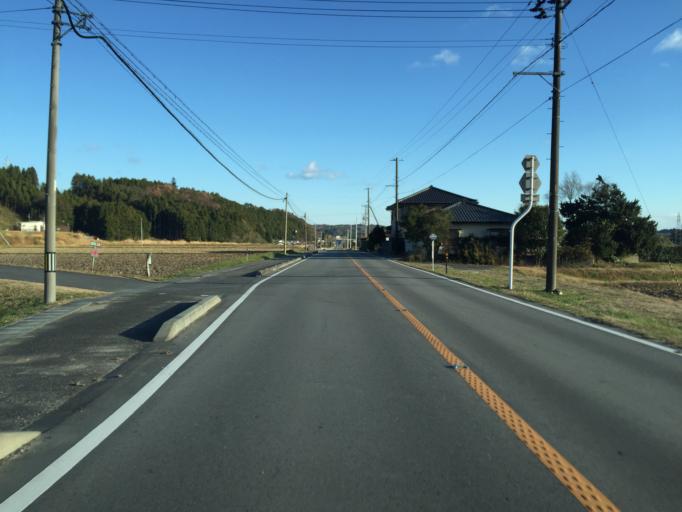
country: JP
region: Fukushima
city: Iwaki
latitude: 37.1403
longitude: 140.8442
